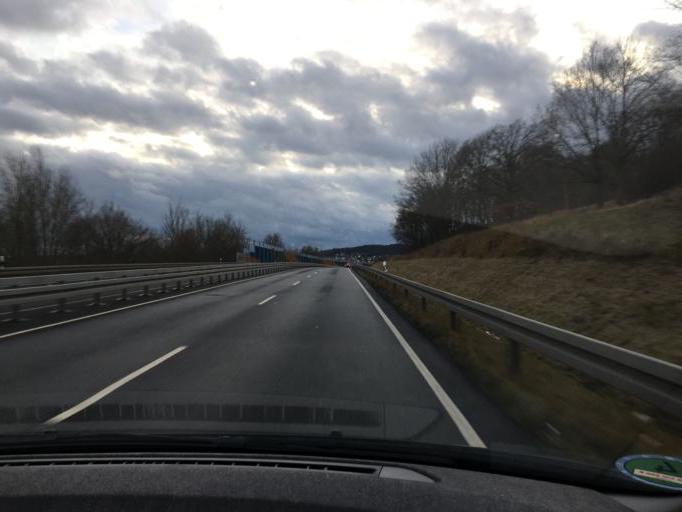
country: DE
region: North Rhine-Westphalia
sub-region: Regierungsbezirk Koln
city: Mechernich
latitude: 50.6231
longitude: 6.6661
